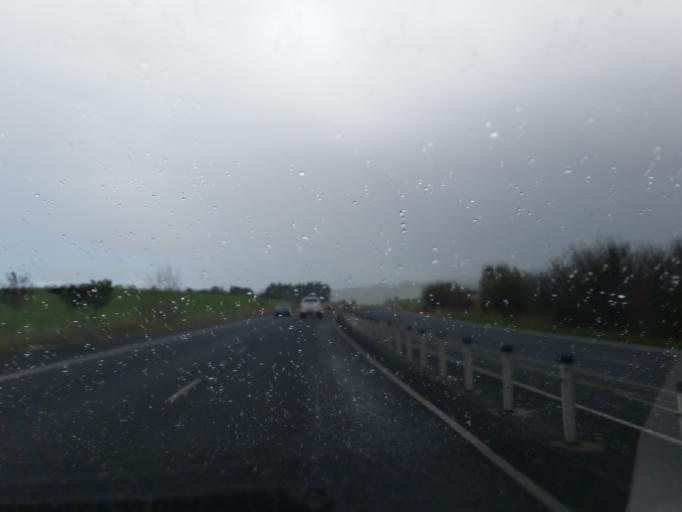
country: NZ
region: Waikato
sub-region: Waikato District
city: Te Kauwhata
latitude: -37.2789
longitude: 175.2958
